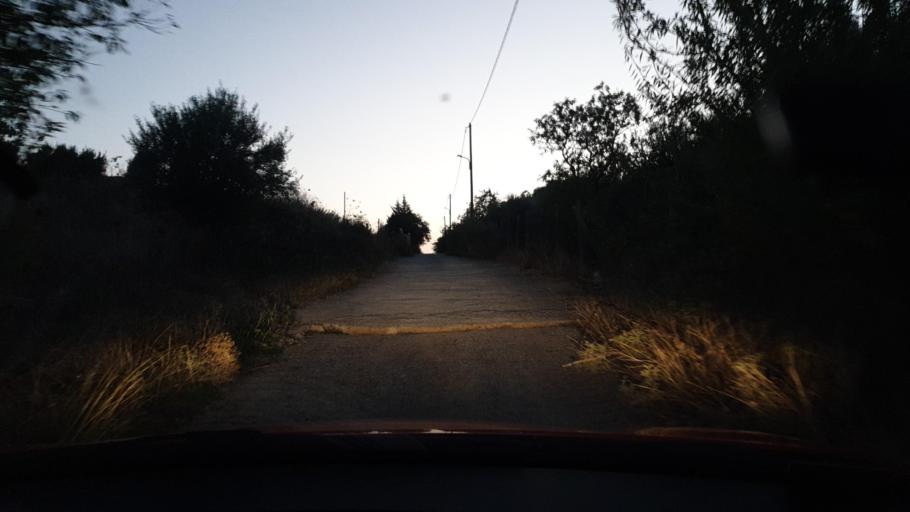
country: GR
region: Central Macedonia
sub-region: Nomos Thessalonikis
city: Agia Triada
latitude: 40.5039
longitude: 22.8347
